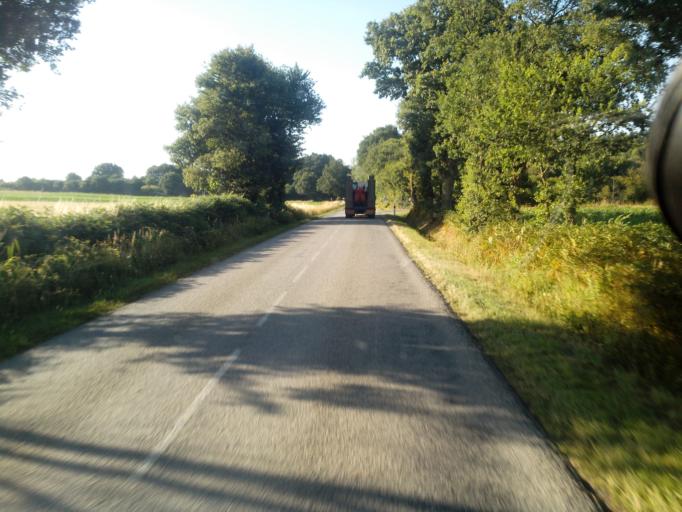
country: FR
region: Brittany
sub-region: Departement du Morbihan
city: Loyat
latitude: 48.0045
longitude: -2.3912
